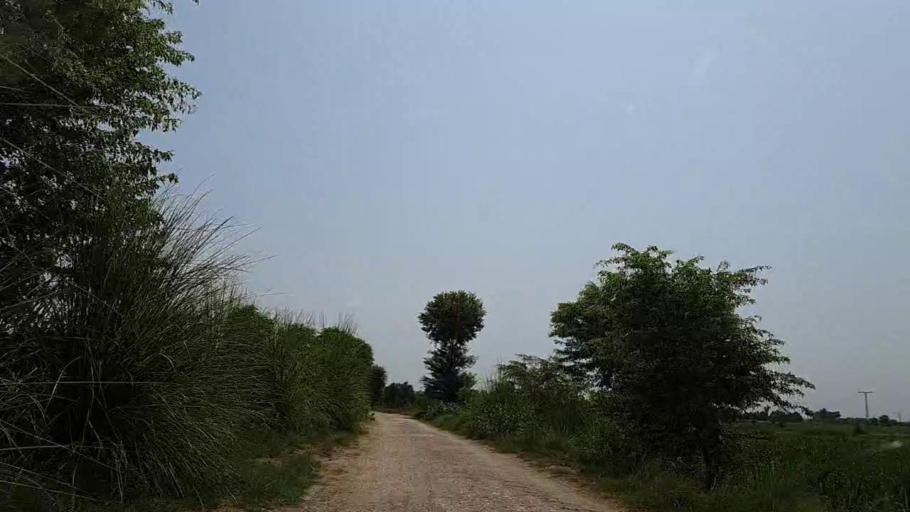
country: PK
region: Sindh
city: Adilpur
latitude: 27.9358
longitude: 69.3934
